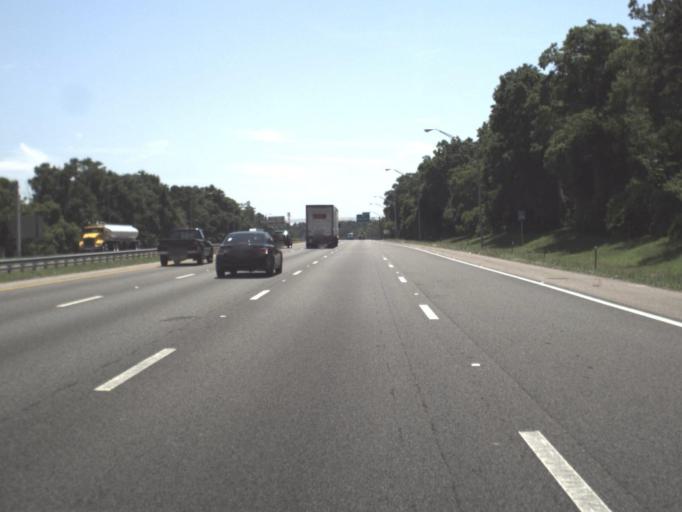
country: US
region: Florida
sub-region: Clay County
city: Bellair-Meadowbrook Terrace
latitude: 30.2913
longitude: -81.7714
